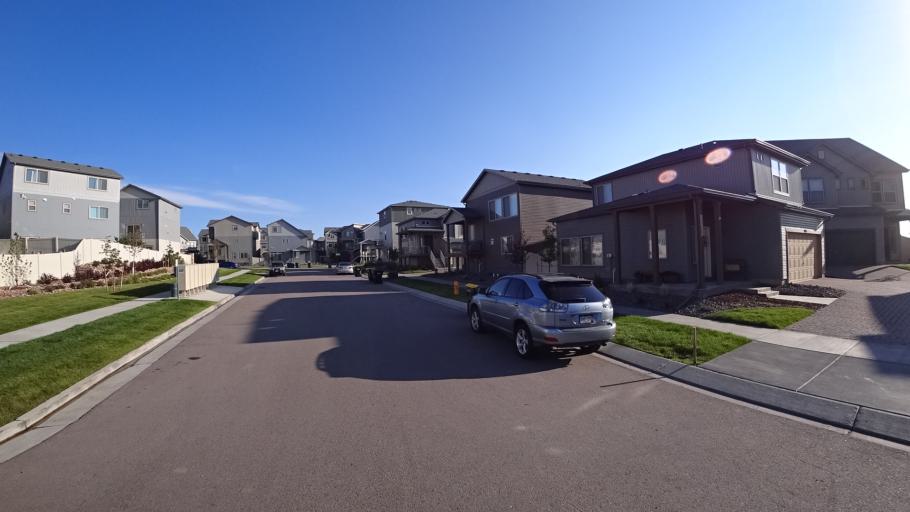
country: US
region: Colorado
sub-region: El Paso County
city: Cimarron Hills
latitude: 38.9271
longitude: -104.6538
